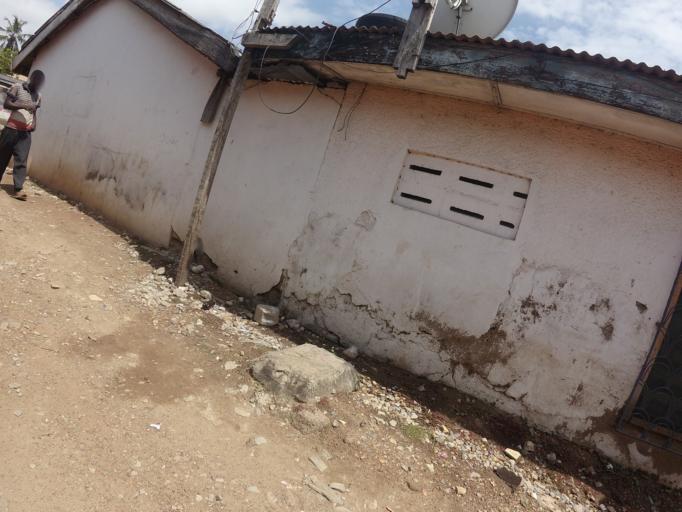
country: GH
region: Greater Accra
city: Accra
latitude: 5.5887
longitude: -0.2028
